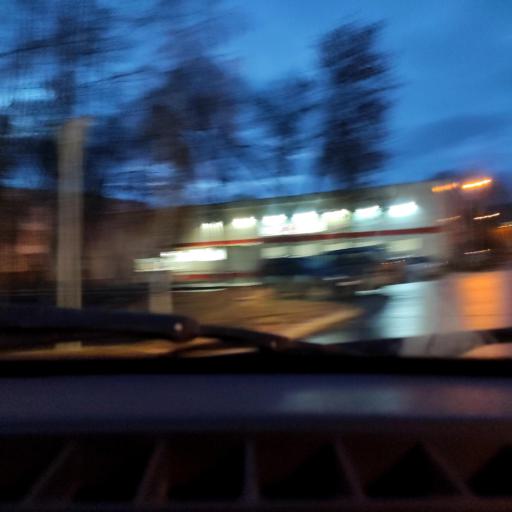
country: RU
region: Bashkortostan
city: Mikhaylovka
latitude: 54.6992
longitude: 55.8361
